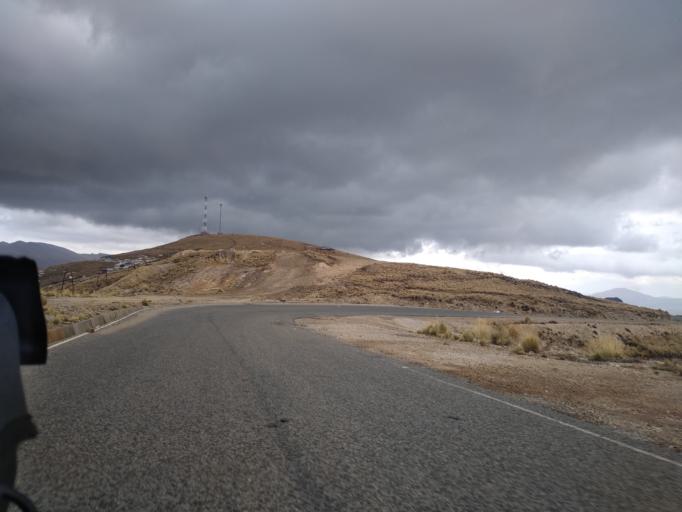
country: PE
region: La Libertad
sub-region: Provincia de Santiago de Chuco
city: Quiruvilca
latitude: -7.9951
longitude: -78.3067
